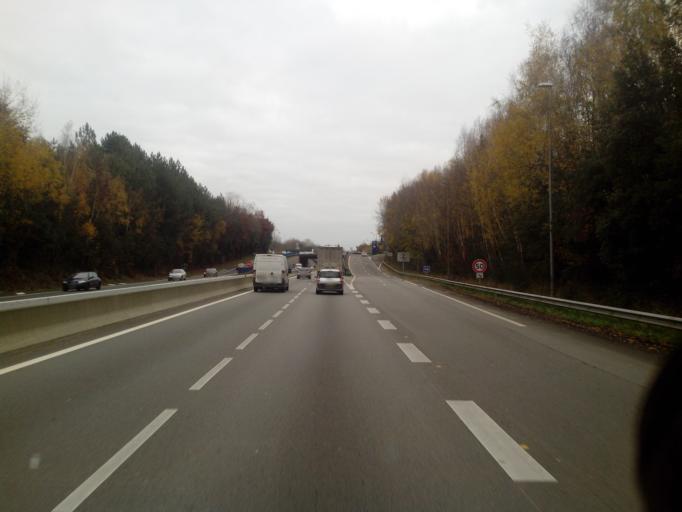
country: FR
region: Pays de la Loire
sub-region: Departement de la Loire-Atlantique
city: Nantes
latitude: 47.2552
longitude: -1.5336
